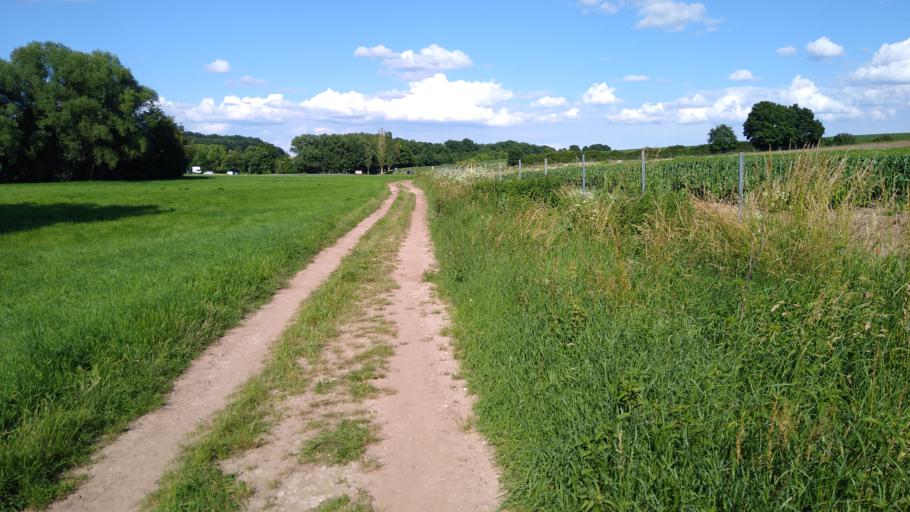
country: DE
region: Bavaria
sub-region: Regierungsbezirk Mittelfranken
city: Obermichelbach
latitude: 49.5067
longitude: 10.9339
